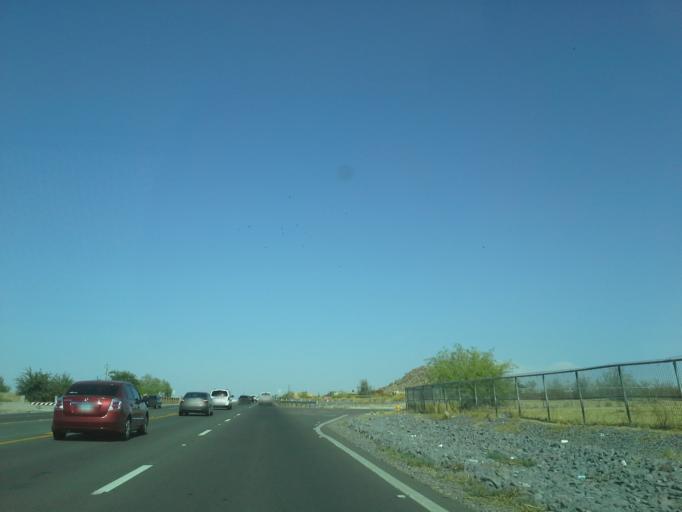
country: US
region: Arizona
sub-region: Maricopa County
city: Queen Creek
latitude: 33.2006
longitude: -111.6262
